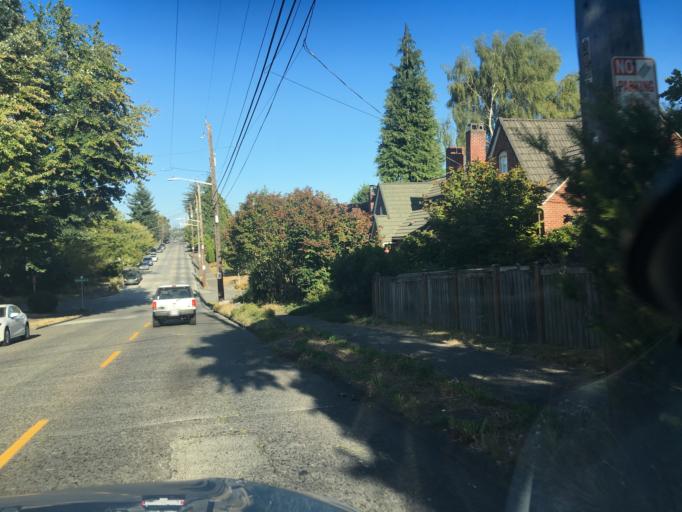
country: US
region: Washington
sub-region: King County
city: Shoreline
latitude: 47.6869
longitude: -122.3536
